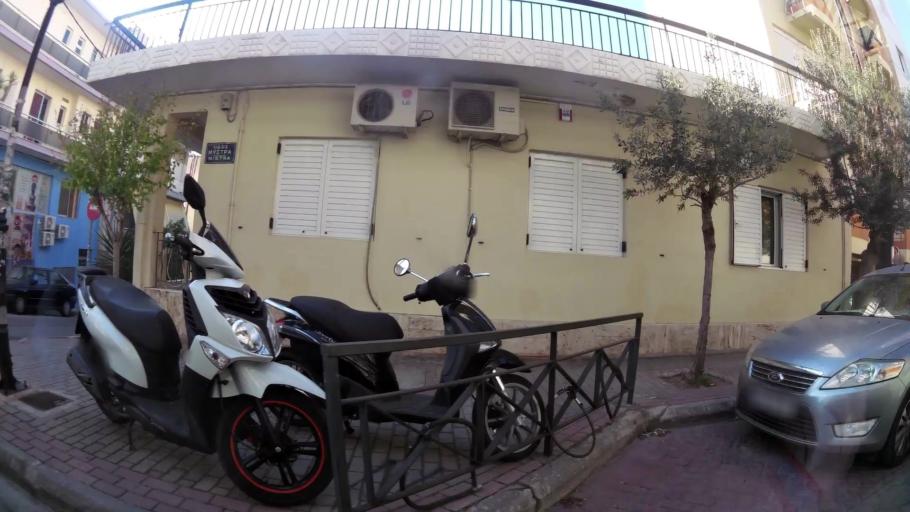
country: GR
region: Attica
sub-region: Nomos Piraios
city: Keratsini
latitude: 37.9707
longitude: 23.6271
